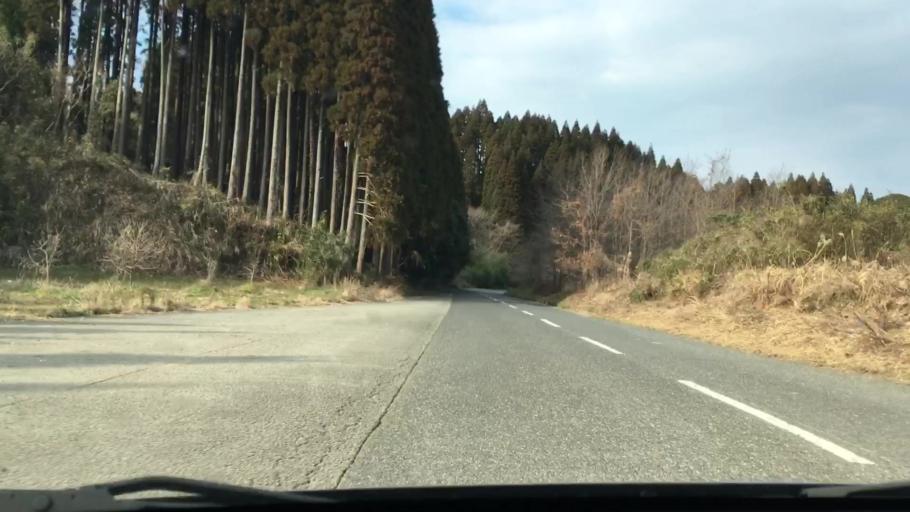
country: JP
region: Miyazaki
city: Nichinan
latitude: 31.6199
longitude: 131.3365
